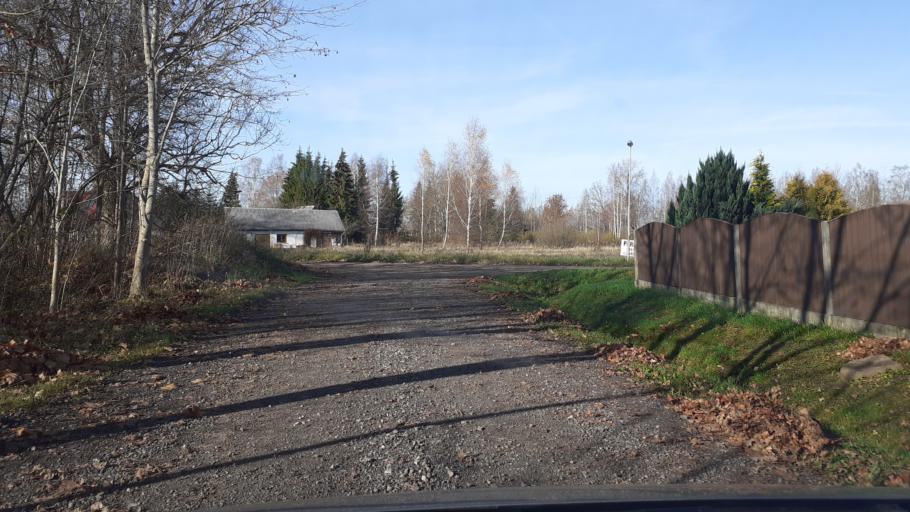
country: LV
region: Kuldigas Rajons
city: Kuldiga
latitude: 56.9581
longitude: 21.9965
